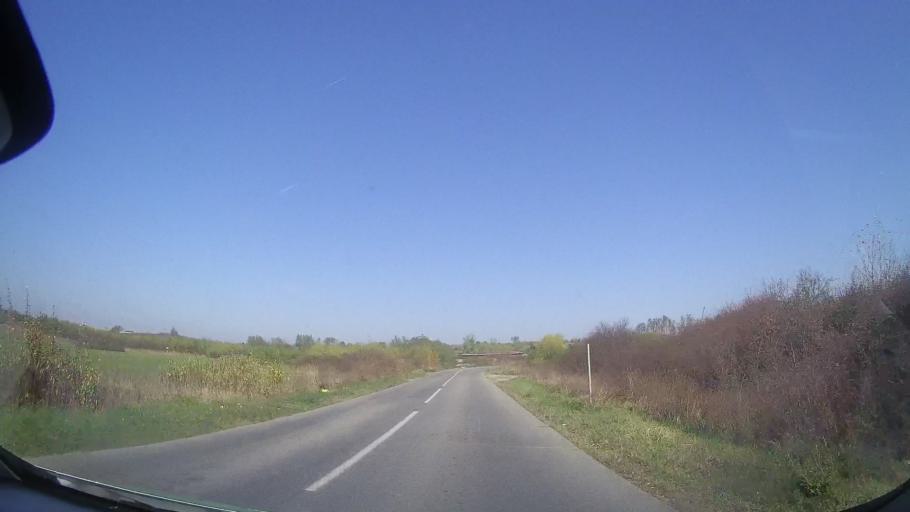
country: RO
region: Timis
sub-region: Comuna Costeiu
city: Costeiu
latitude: 45.7514
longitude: 21.8467
